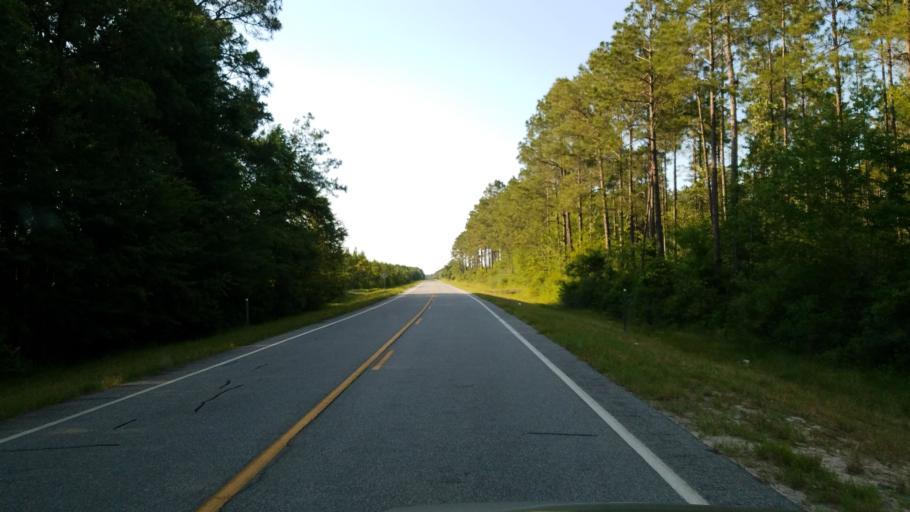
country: US
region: Georgia
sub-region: Echols County
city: Statenville
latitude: 30.8612
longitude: -83.0517
